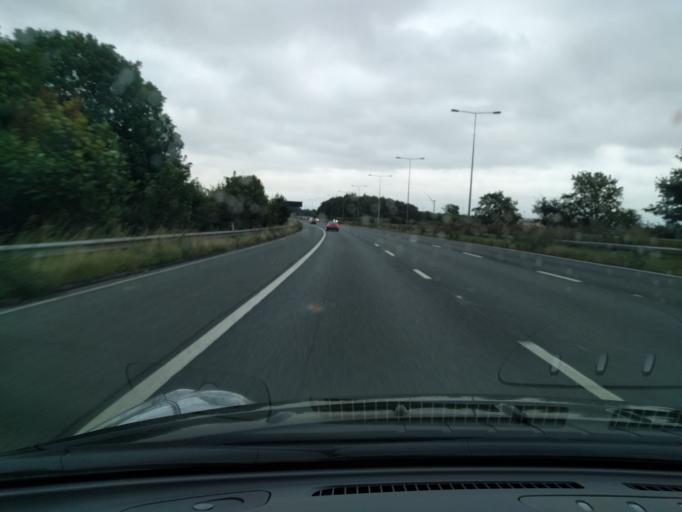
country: GB
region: England
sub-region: Borough of Wigan
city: Ashton in Makerfield
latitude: 53.4670
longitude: -2.6292
